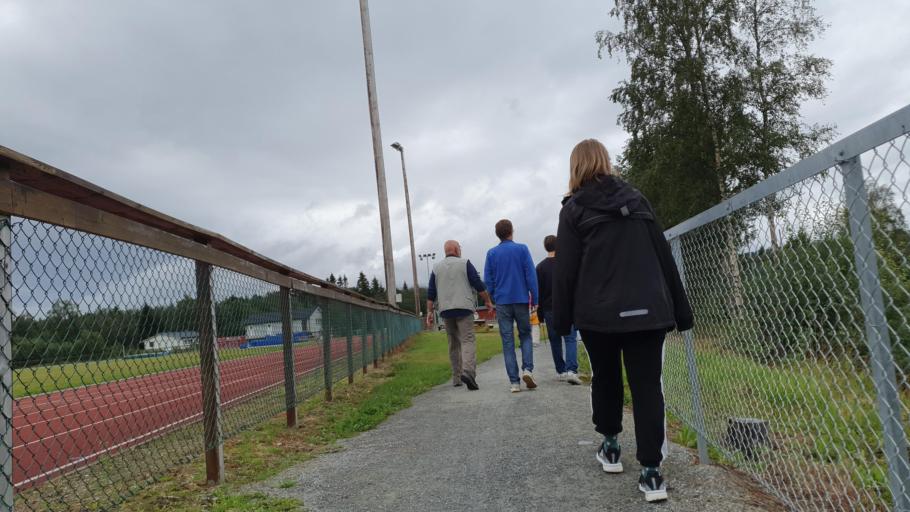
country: NO
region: Sor-Trondelag
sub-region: Selbu
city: Mebonden
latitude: 63.2264
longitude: 11.0232
